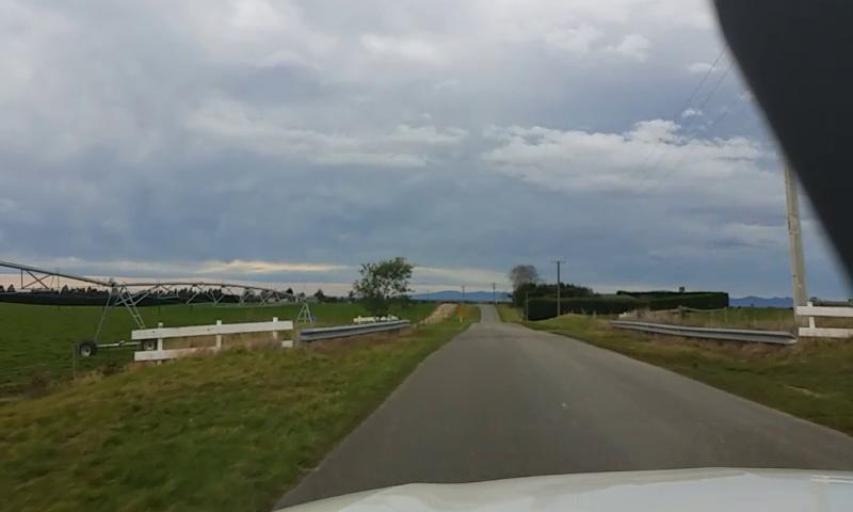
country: NZ
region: Canterbury
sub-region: Waimakariri District
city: Kaiapoi
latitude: -43.2948
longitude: 172.4743
